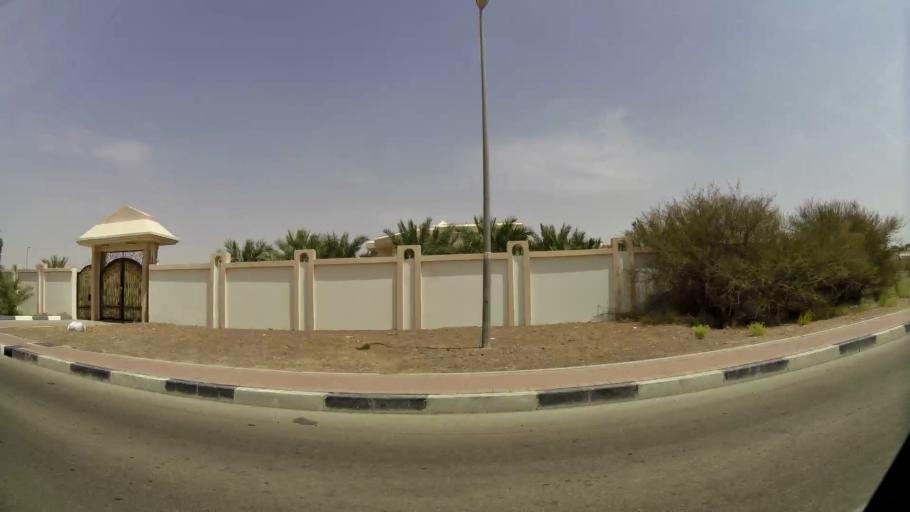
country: AE
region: Abu Dhabi
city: Al Ain
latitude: 24.1798
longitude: 55.7203
